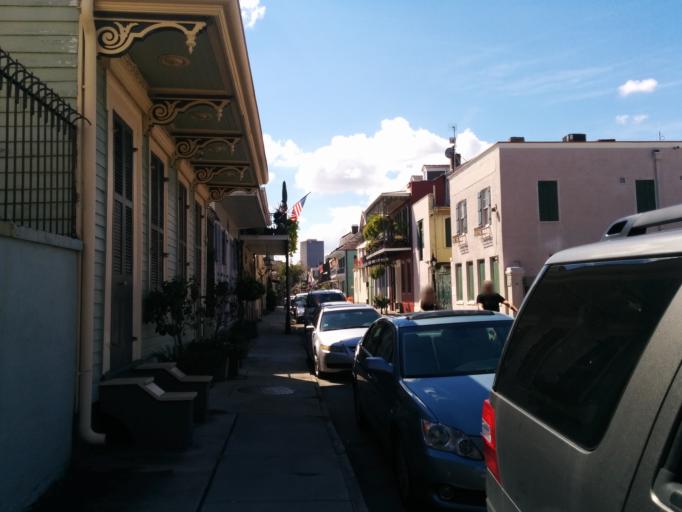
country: US
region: Louisiana
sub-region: Orleans Parish
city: New Orleans
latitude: 29.9629
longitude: -90.0646
